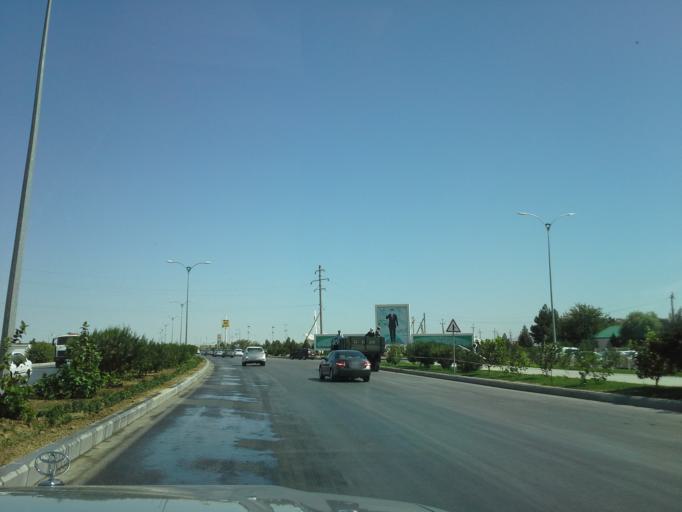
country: TM
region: Ahal
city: Annau
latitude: 37.9078
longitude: 58.5102
